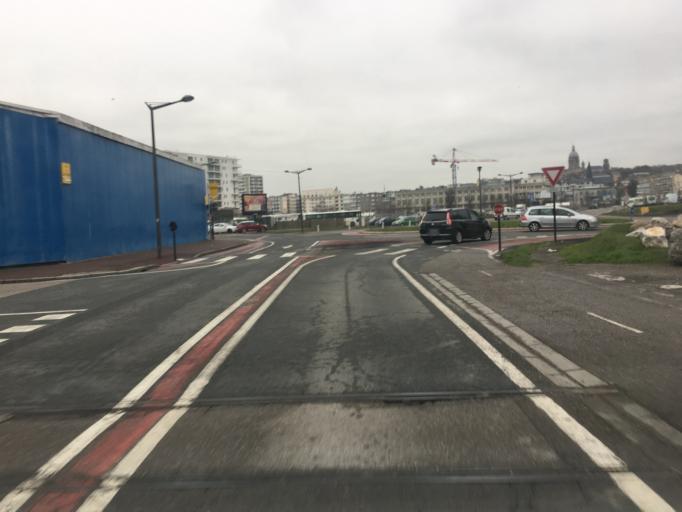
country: FR
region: Nord-Pas-de-Calais
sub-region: Departement du Pas-de-Calais
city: Outreau
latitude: 50.7203
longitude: 1.5985
